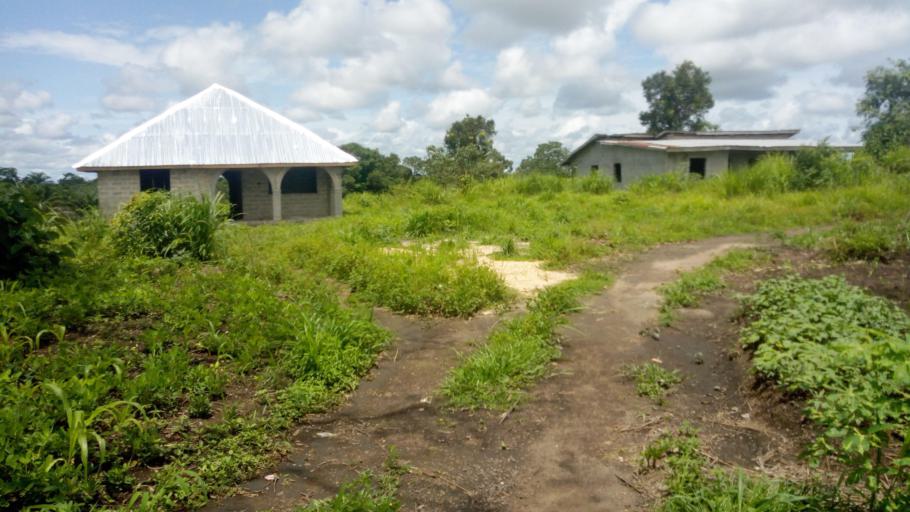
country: SL
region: Northern Province
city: Magburaka
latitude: 8.7111
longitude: -11.9538
